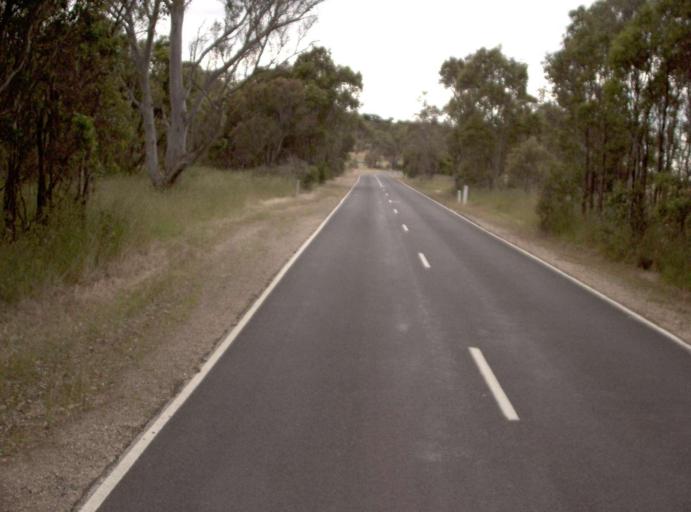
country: AU
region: Victoria
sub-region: East Gippsland
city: Bairnsdale
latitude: -37.9811
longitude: 147.4115
